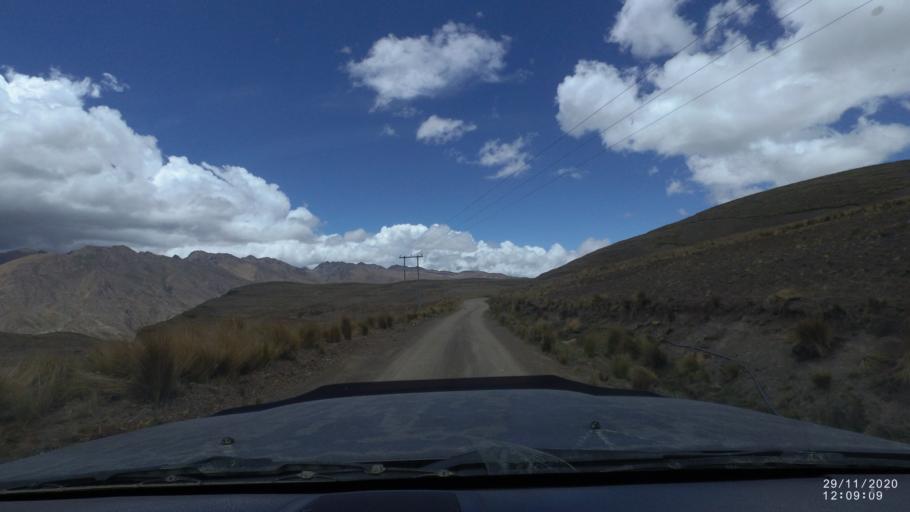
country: BO
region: Cochabamba
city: Cochabamba
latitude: -17.1320
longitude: -66.3025
